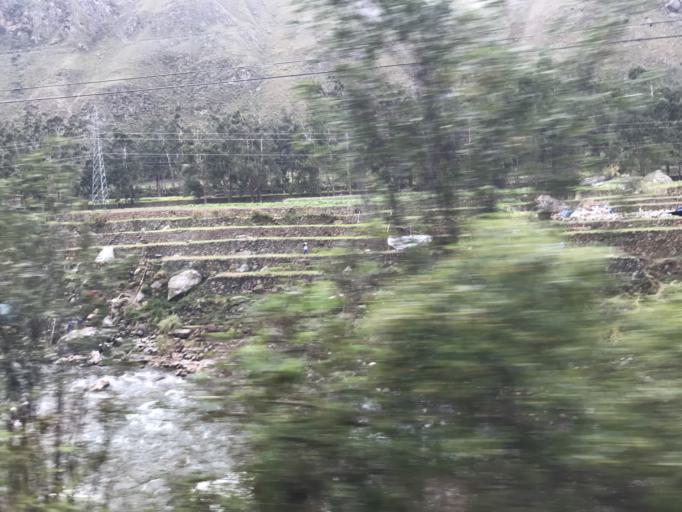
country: PE
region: Cusco
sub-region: Provincia de La Convencion
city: Santa Teresa
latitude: -13.2242
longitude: -72.4403
